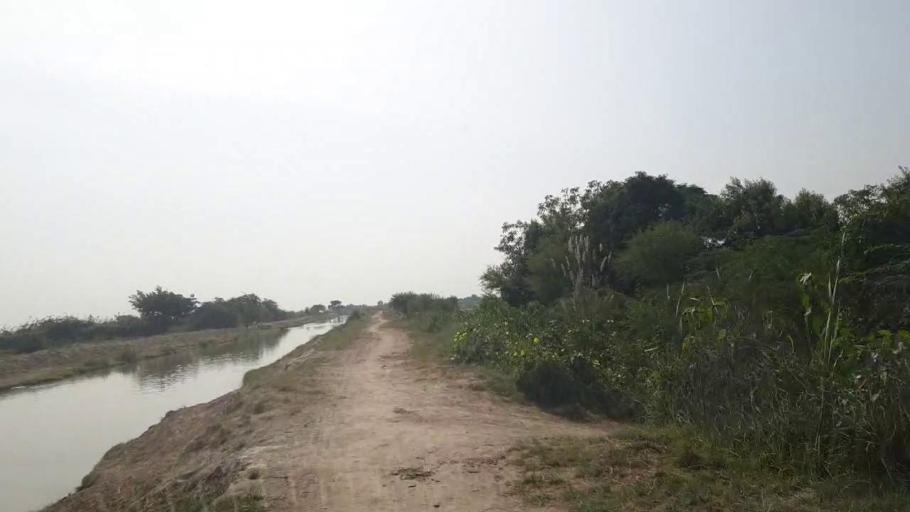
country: PK
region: Sindh
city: Badin
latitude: 24.5598
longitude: 68.8497
